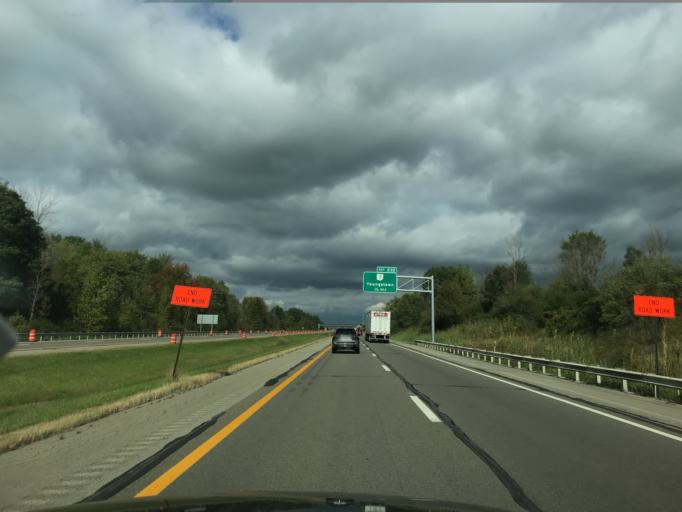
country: US
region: Ohio
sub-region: Mahoning County
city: Boardman
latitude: 40.9591
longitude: -80.6441
